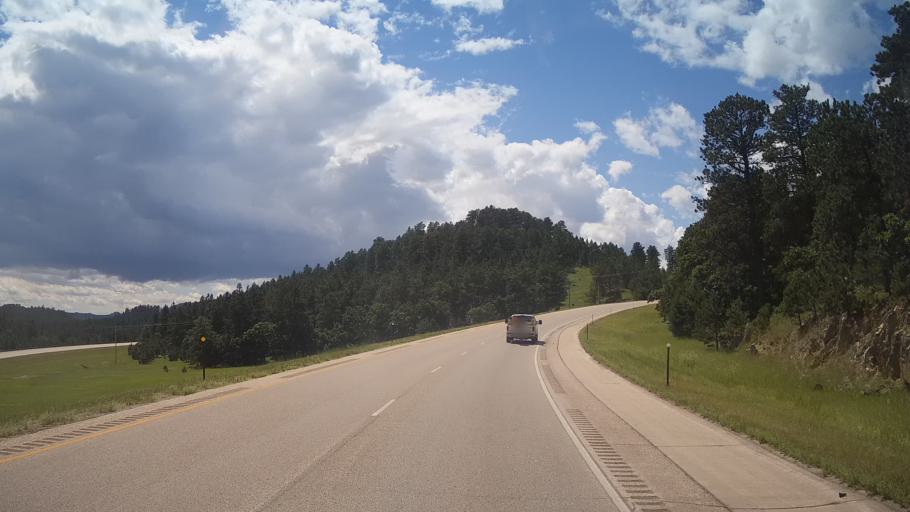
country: US
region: South Dakota
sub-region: Pennington County
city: Colonial Pine Hills
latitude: 43.9429
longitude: -103.3768
